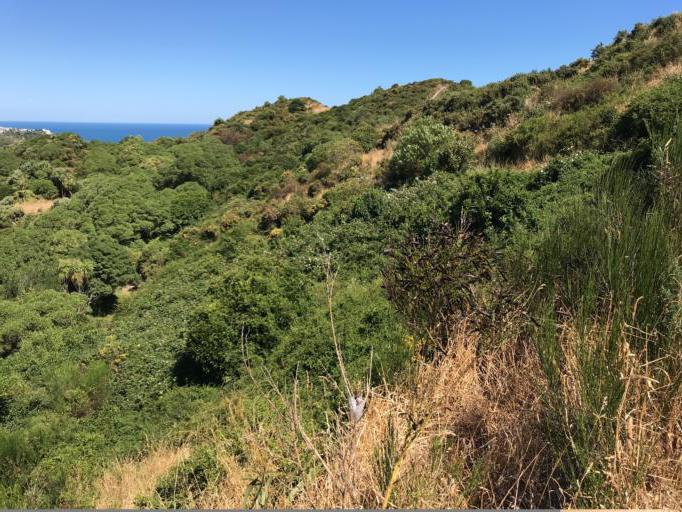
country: NZ
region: Wellington
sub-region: Wellington City
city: Brooklyn
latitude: -41.3309
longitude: 174.7664
